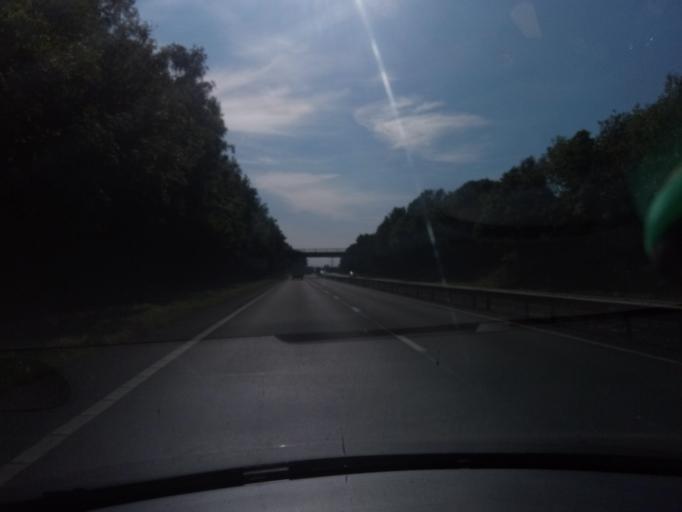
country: GB
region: England
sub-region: North Yorkshire
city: Thirsk
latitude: 54.2834
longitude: -1.3406
